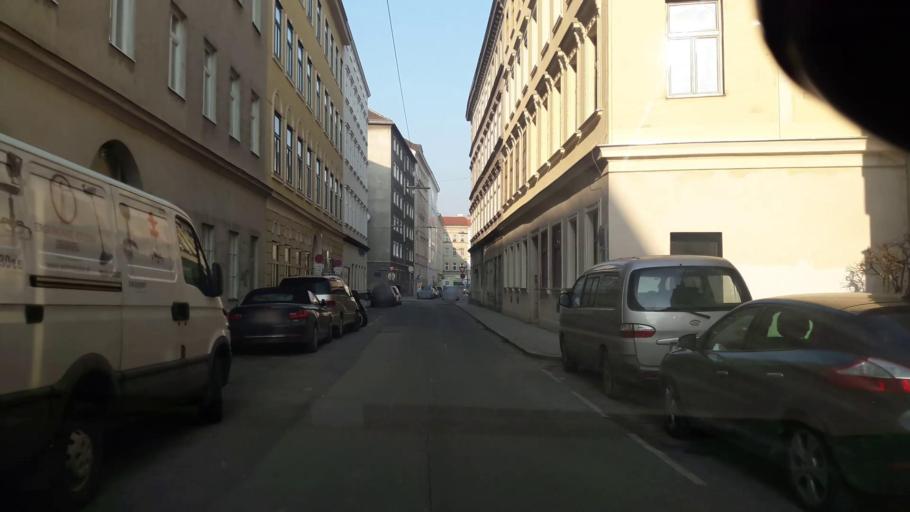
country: AT
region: Vienna
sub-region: Wien Stadt
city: Vienna
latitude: 48.2168
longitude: 16.3830
